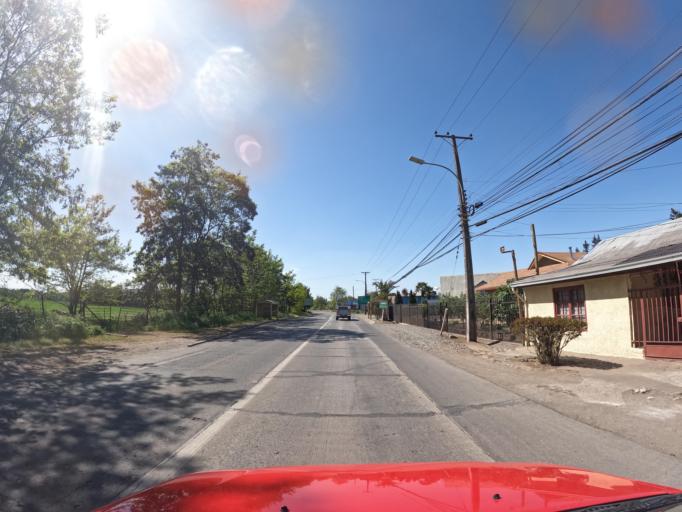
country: CL
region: Maule
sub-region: Provincia de Curico
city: Molina
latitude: -35.0697
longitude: -71.2555
